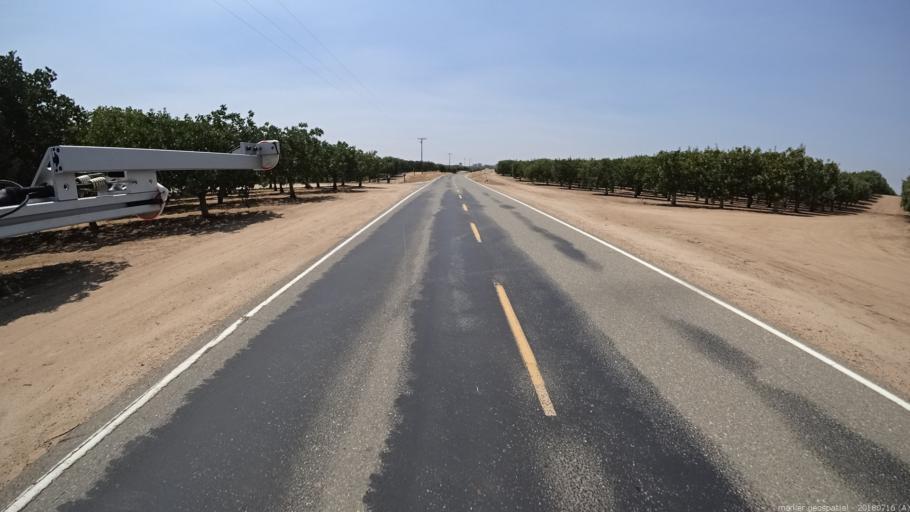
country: US
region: California
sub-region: Madera County
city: Madera Acres
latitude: 37.0643
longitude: -119.9769
